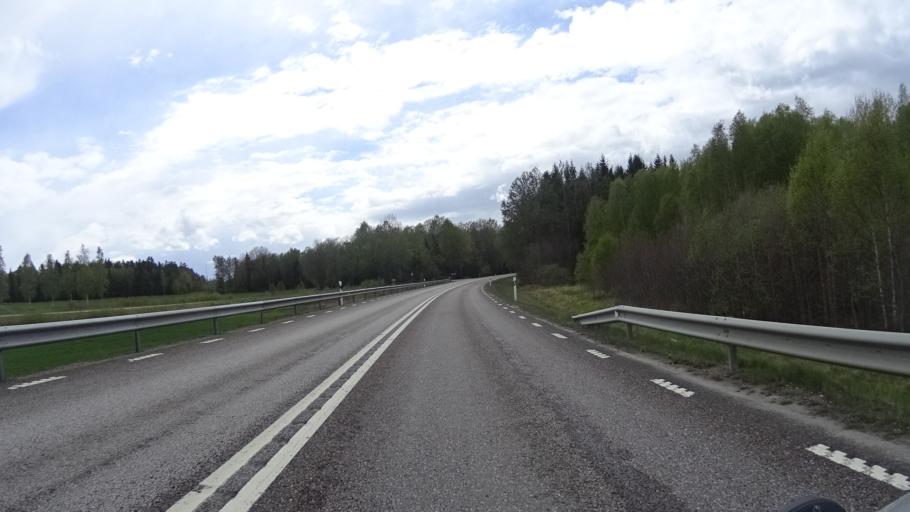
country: SE
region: Vaestra Goetaland
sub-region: Karlsborgs Kommun
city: Karlsborg
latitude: 58.4999
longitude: 14.4614
